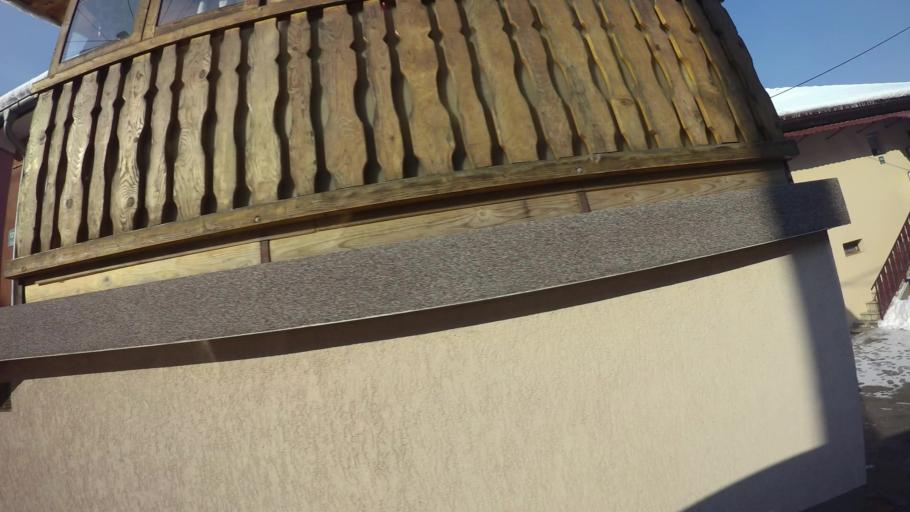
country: BA
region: Federation of Bosnia and Herzegovina
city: Kobilja Glava
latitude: 43.8462
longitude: 18.4030
